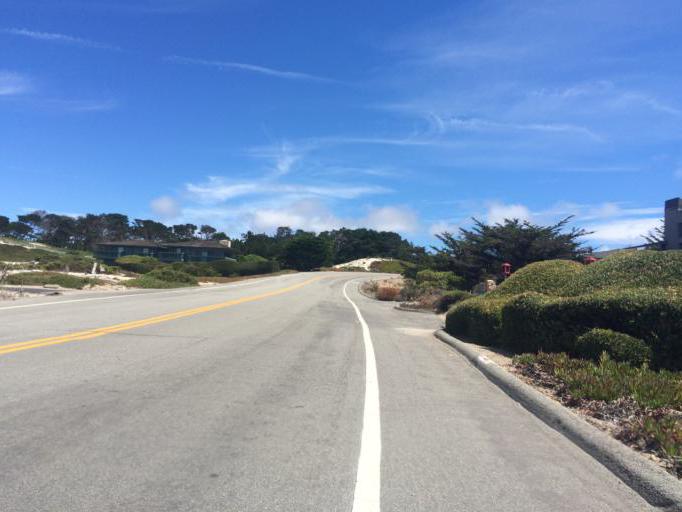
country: US
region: California
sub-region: Monterey County
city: Del Monte Forest
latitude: 36.5867
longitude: -121.9633
